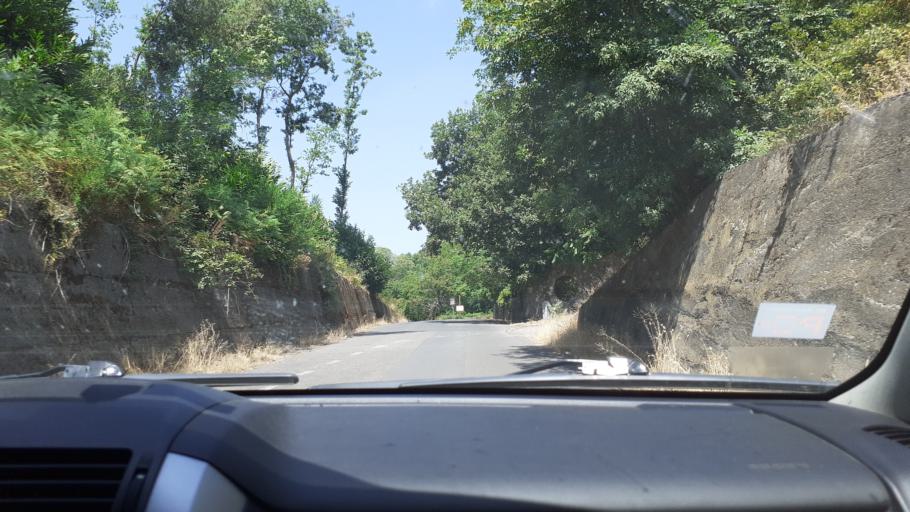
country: IT
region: Sicily
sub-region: Catania
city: Nicolosi
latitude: 37.6370
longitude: 15.0228
